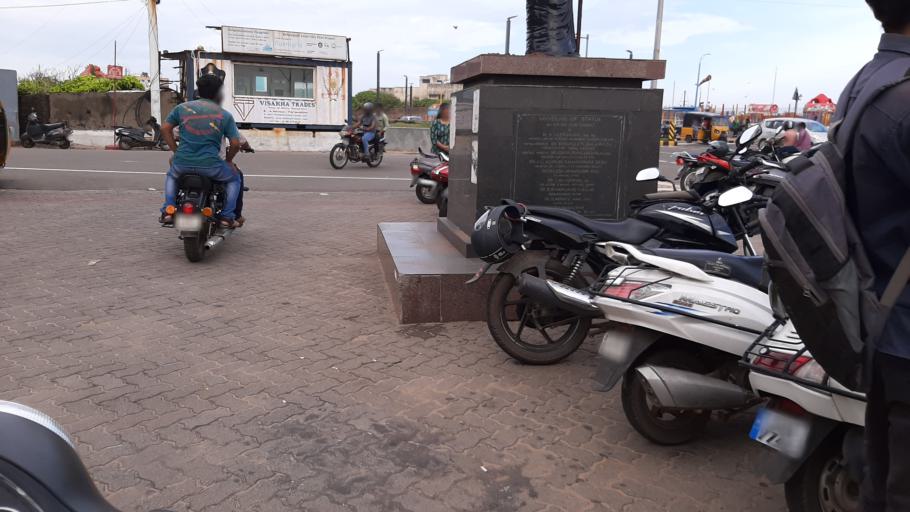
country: IN
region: Andhra Pradesh
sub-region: Vishakhapatnam
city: Yarada
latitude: 17.7193
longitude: 83.3336
